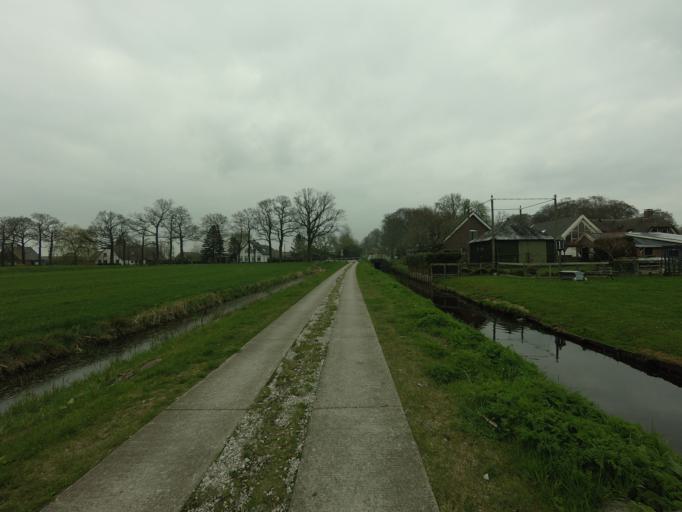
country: NL
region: Utrecht
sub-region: Gemeente De Bilt
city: De Bilt
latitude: 52.1487
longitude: 5.1561
